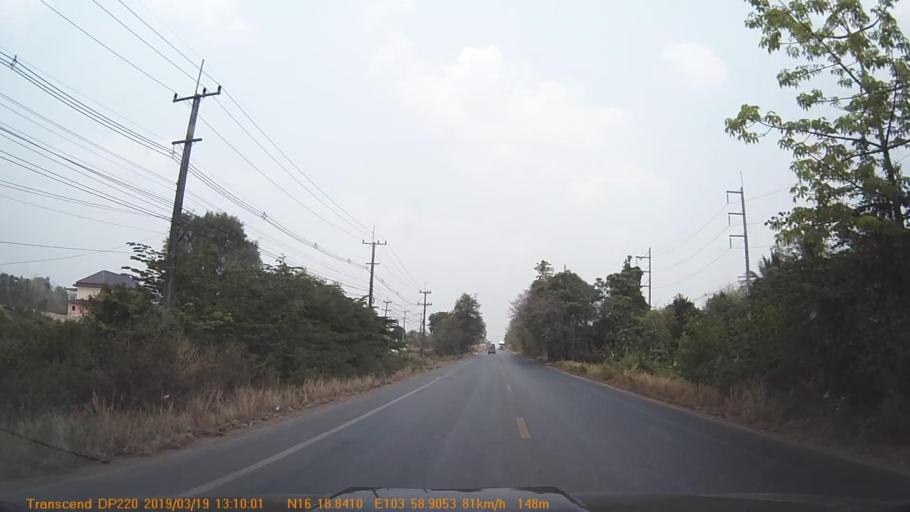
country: TH
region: Roi Et
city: Waeng
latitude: 16.3144
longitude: 103.9818
